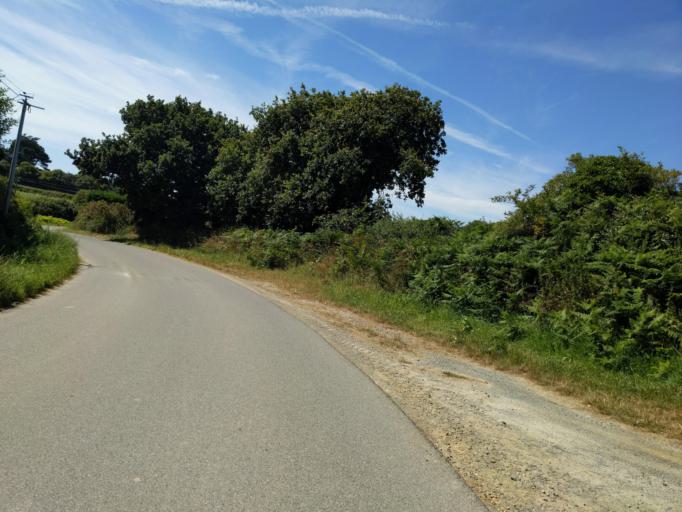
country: FR
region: Brittany
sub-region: Departement des Cotes-d'Armor
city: Pleumeur-Gautier
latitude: 48.8298
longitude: -3.1753
